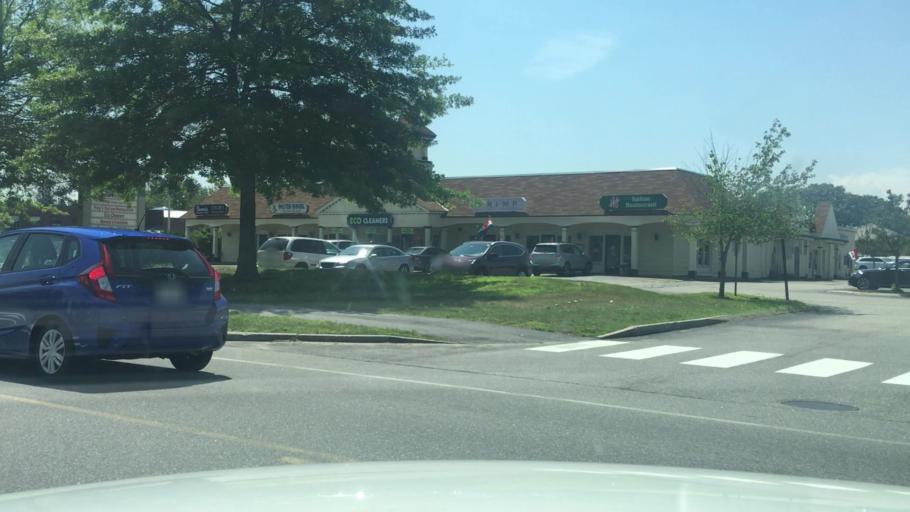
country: US
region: Maine
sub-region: Cumberland County
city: Falmouth
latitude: 43.7199
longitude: -70.2328
